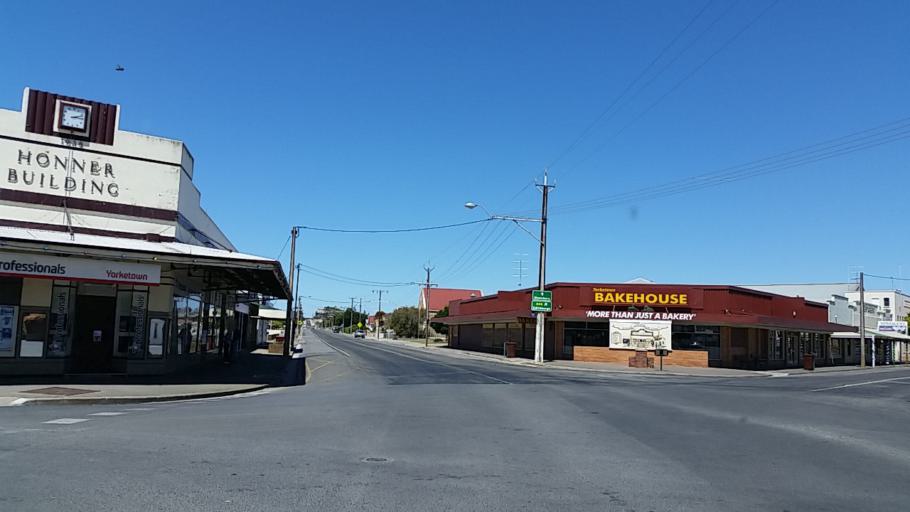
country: AU
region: South Australia
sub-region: Yorke Peninsula
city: Honiton
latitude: -35.0189
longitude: 137.6055
